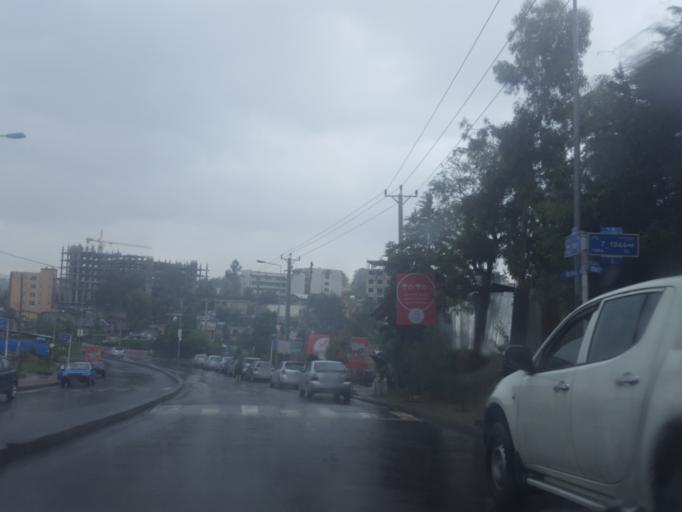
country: ET
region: Adis Abeba
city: Addis Ababa
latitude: 9.0285
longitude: 38.7819
